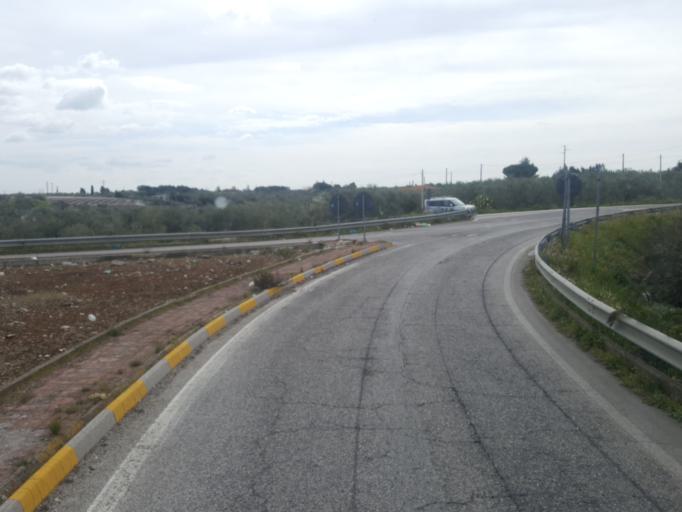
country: IT
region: Apulia
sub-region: Provincia di Barletta - Andria - Trani
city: Bisceglie
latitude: 41.2228
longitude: 16.5067
